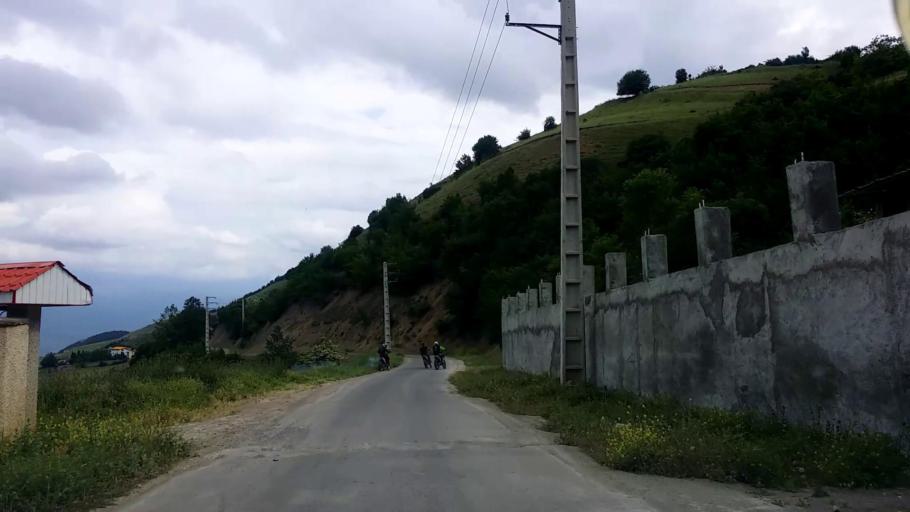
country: IR
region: Mazandaran
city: Chalus
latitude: 36.5506
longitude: 51.2700
